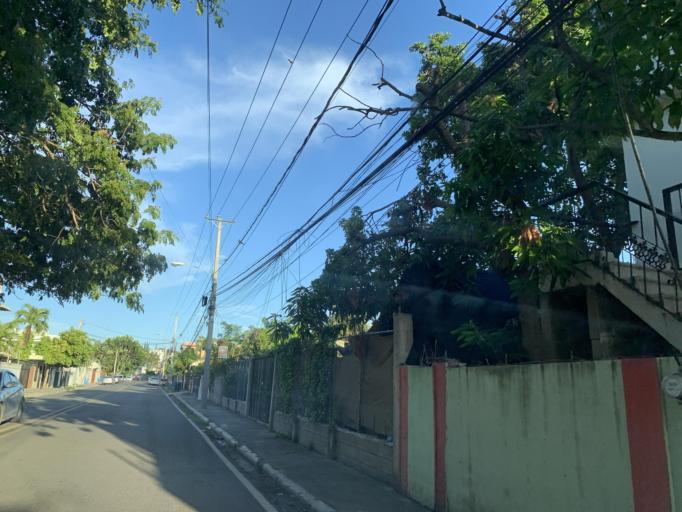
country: DO
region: Santiago
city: Santiago de los Caballeros
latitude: 19.4699
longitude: -70.6949
